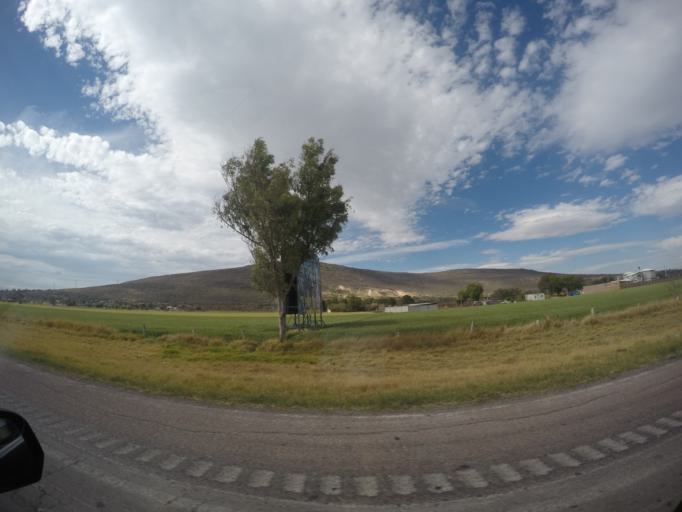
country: MX
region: Guanajuato
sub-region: Salamanca
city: Zapote de Palomas
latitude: 20.5894
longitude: -101.0976
